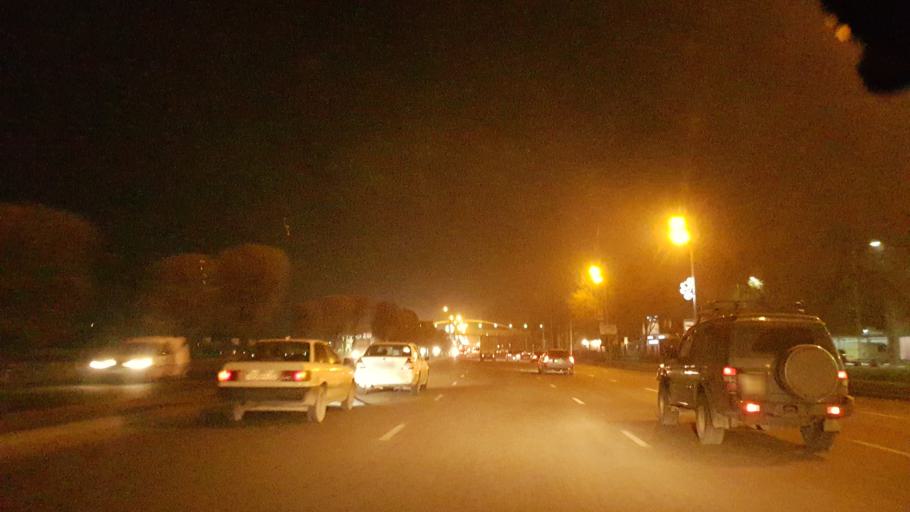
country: KZ
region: Almaty Qalasy
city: Almaty
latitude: 43.2588
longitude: 76.8479
